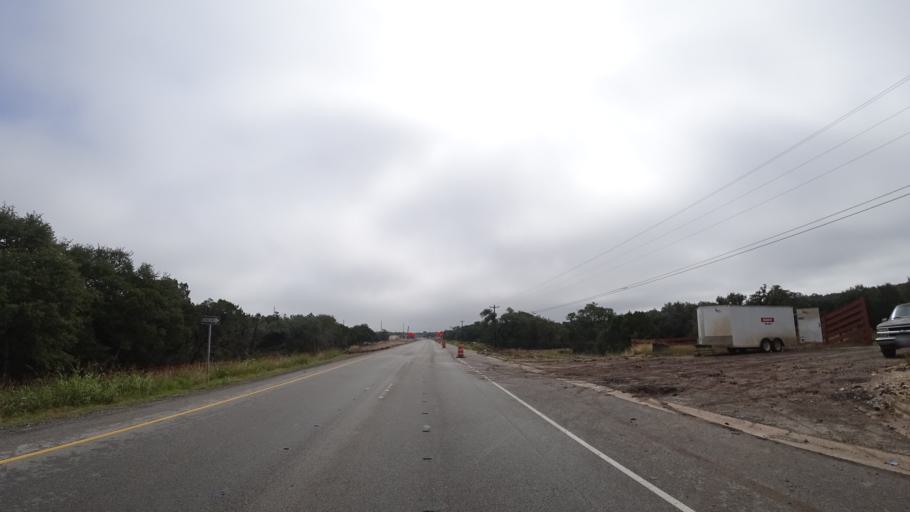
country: US
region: Texas
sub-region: Travis County
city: Shady Hollow
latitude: 30.1763
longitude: -97.8931
